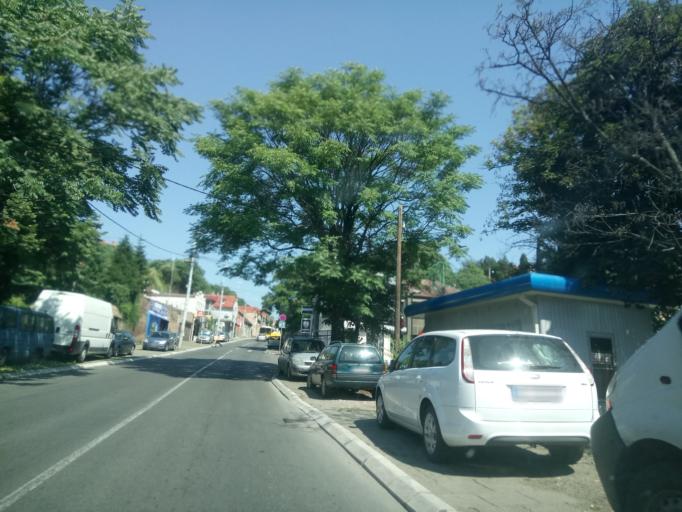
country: RS
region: Central Serbia
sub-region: Belgrade
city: Zemun
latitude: 44.8425
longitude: 20.4048
